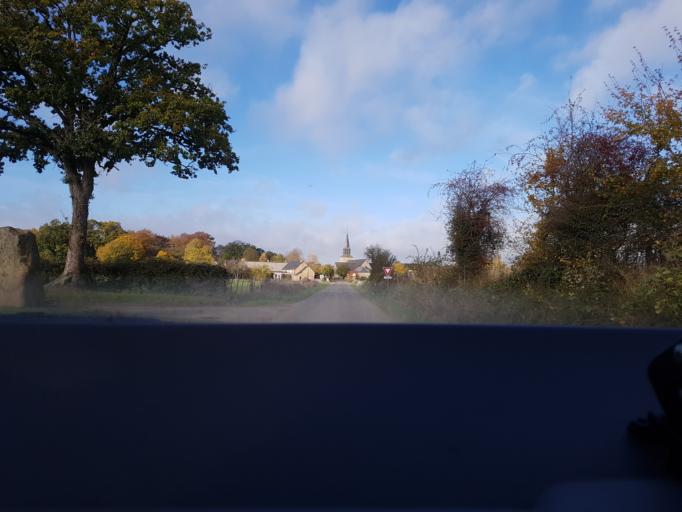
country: FR
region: Pays de la Loire
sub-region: Departement de la Mayenne
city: Ambrieres-les-Vallees
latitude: 48.3841
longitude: -0.5827
